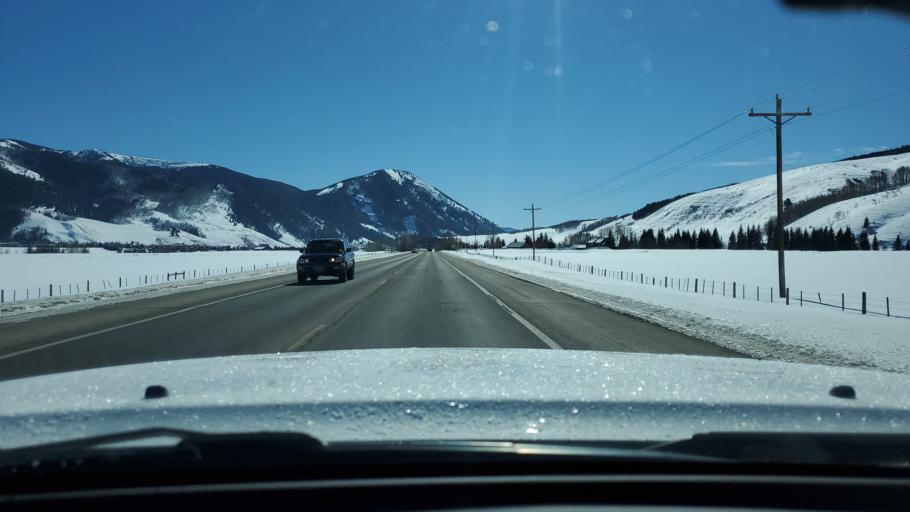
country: US
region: Colorado
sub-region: Gunnison County
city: Crested Butte
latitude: 38.8194
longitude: -106.9110
